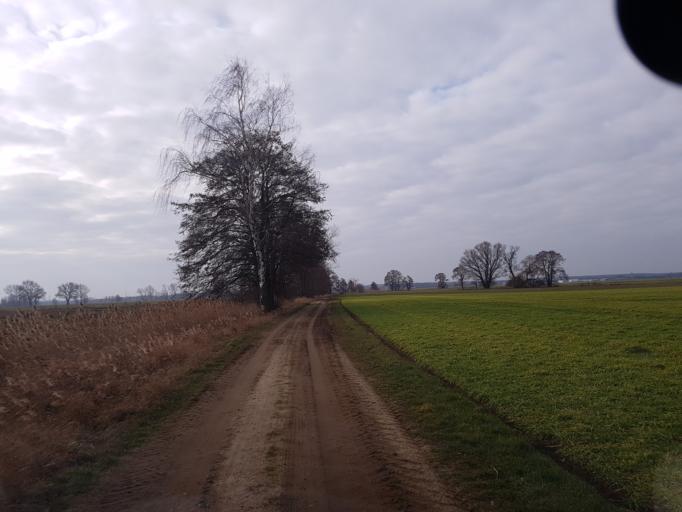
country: DE
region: Brandenburg
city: Schonewalde
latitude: 51.6671
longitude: 13.5703
